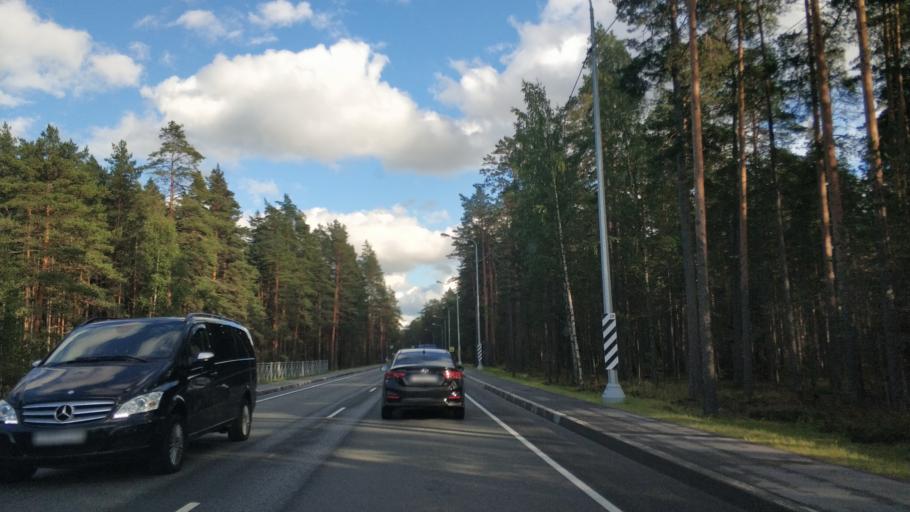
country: RU
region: Leningrad
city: Priozersk
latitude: 61.0125
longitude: 30.1550
